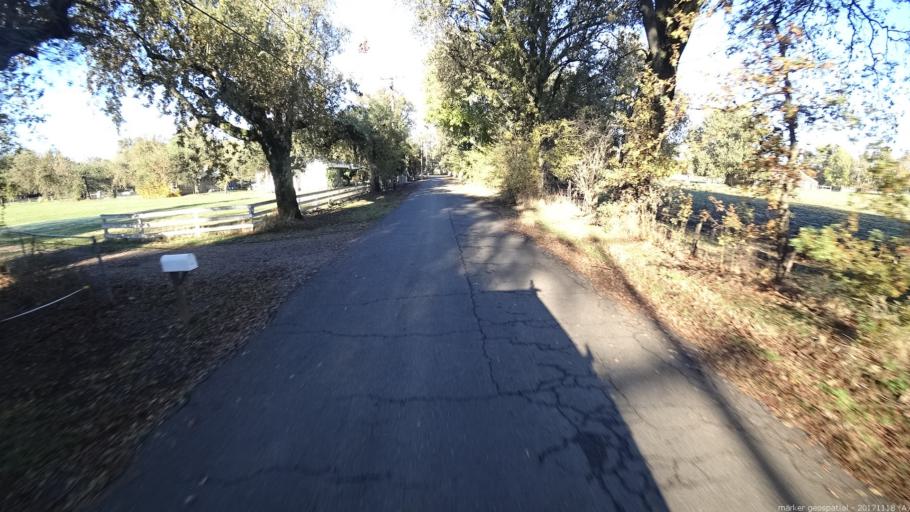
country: US
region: California
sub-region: Shasta County
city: Anderson
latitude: 40.4468
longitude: -122.2751
